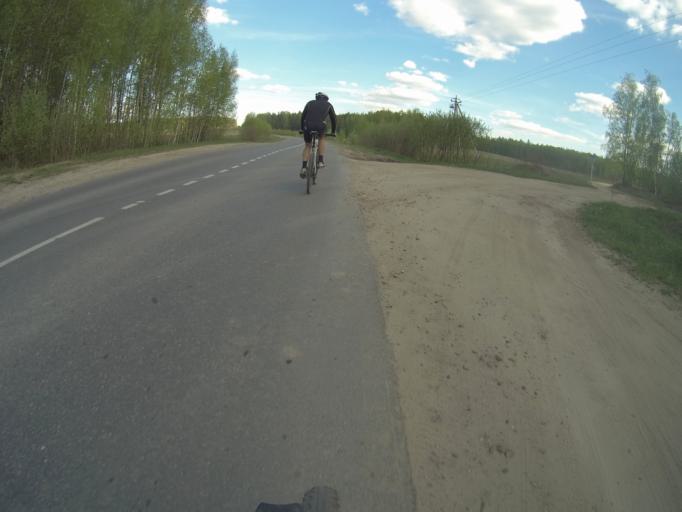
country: RU
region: Vladimir
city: Raduzhnyy
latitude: 55.9903
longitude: 40.2152
